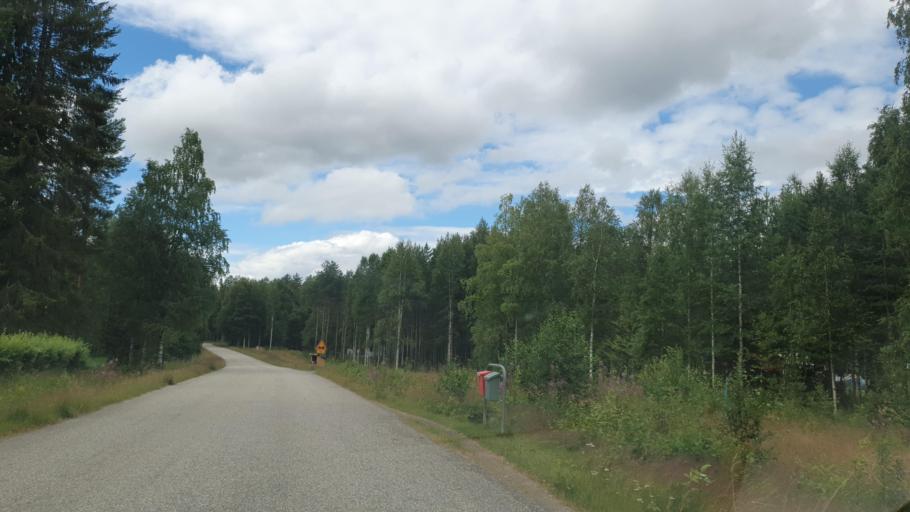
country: FI
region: Kainuu
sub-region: Kehys-Kainuu
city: Kuhmo
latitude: 64.0946
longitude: 29.4269
